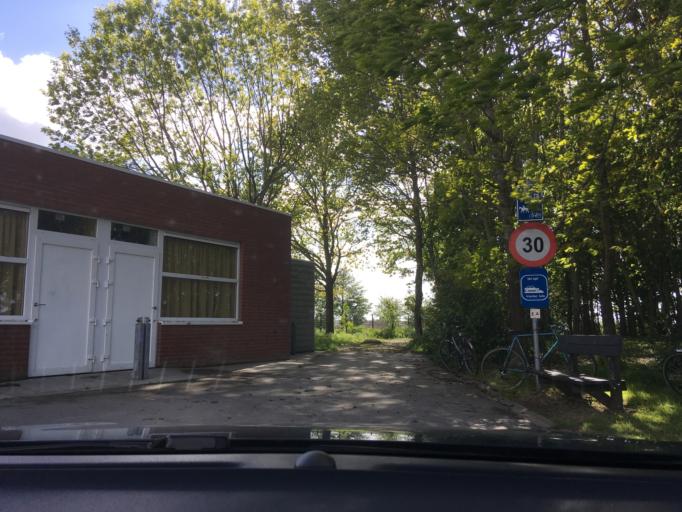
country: BE
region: Flanders
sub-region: Provincie West-Vlaanderen
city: Hooglede
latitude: 50.9945
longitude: 3.0929
